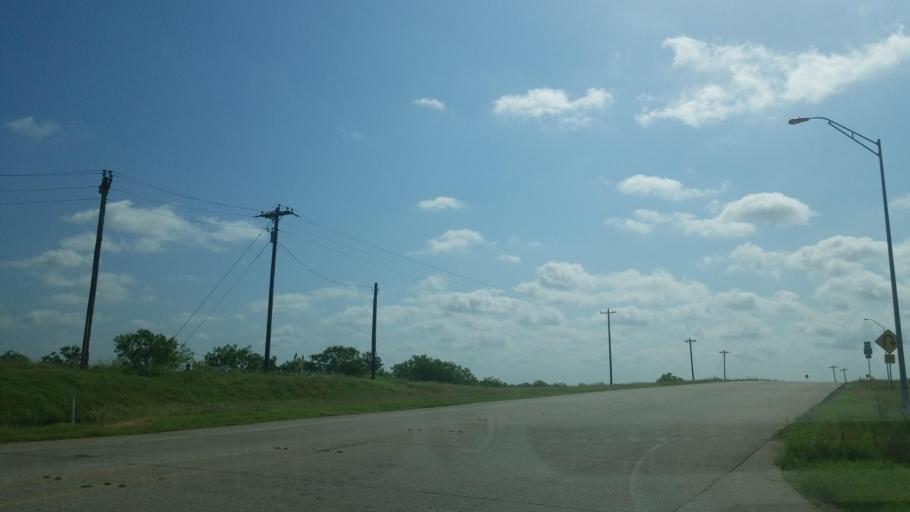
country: US
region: Texas
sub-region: Denton County
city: Denton
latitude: 33.2560
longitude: -97.1769
